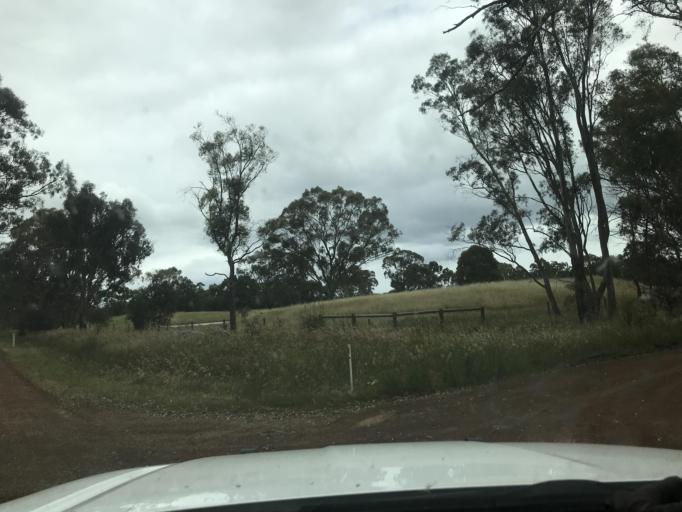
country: AU
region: South Australia
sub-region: Wattle Range
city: Penola
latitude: -37.0826
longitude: 141.2810
